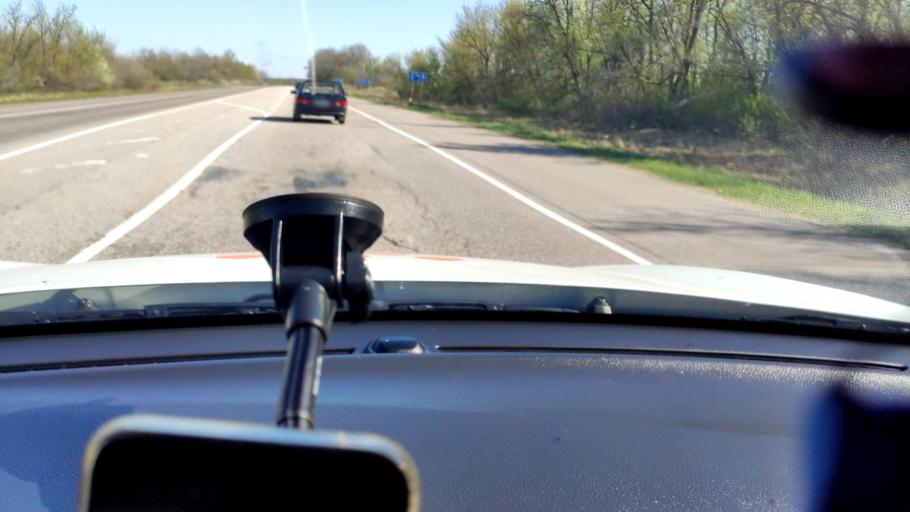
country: RU
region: Voronezj
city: Kolodeznyy
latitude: 51.3112
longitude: 39.0331
